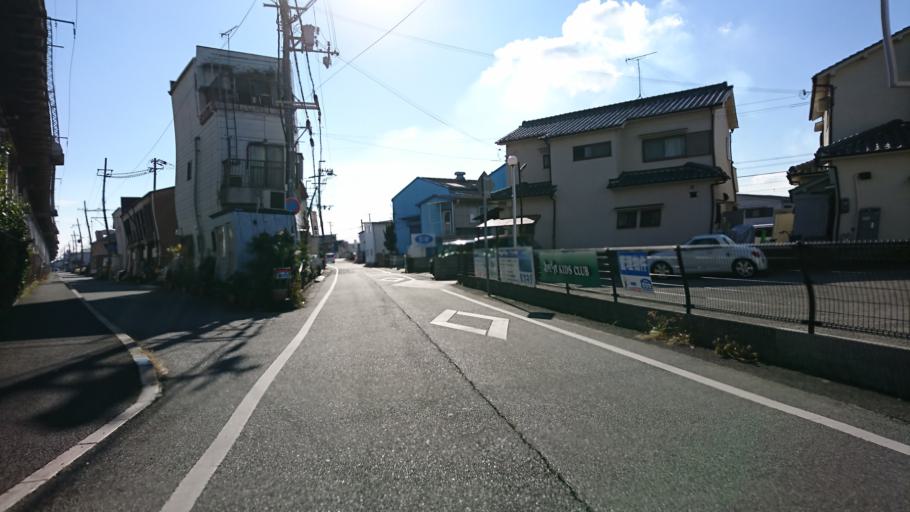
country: JP
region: Hyogo
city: Kakogawacho-honmachi
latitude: 34.7349
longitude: 134.8443
